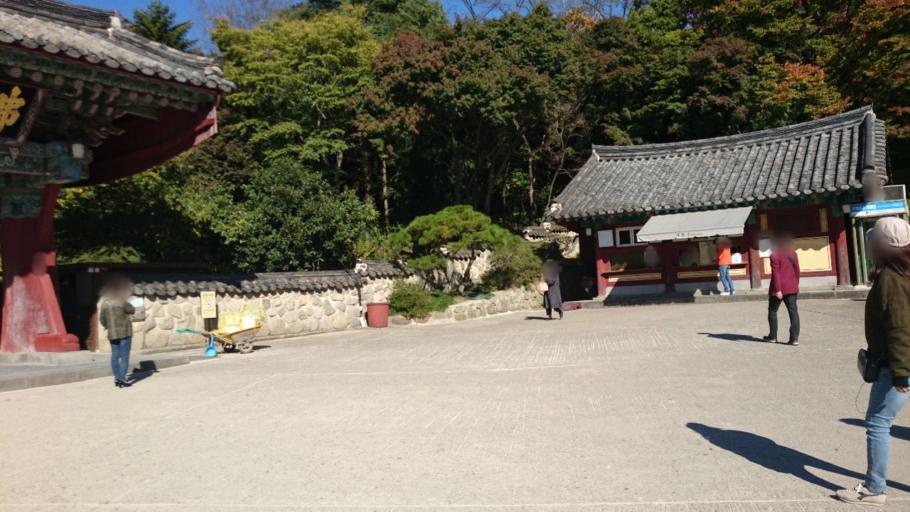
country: KR
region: Gyeongsangbuk-do
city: Kyonju
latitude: 35.7870
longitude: 129.3324
